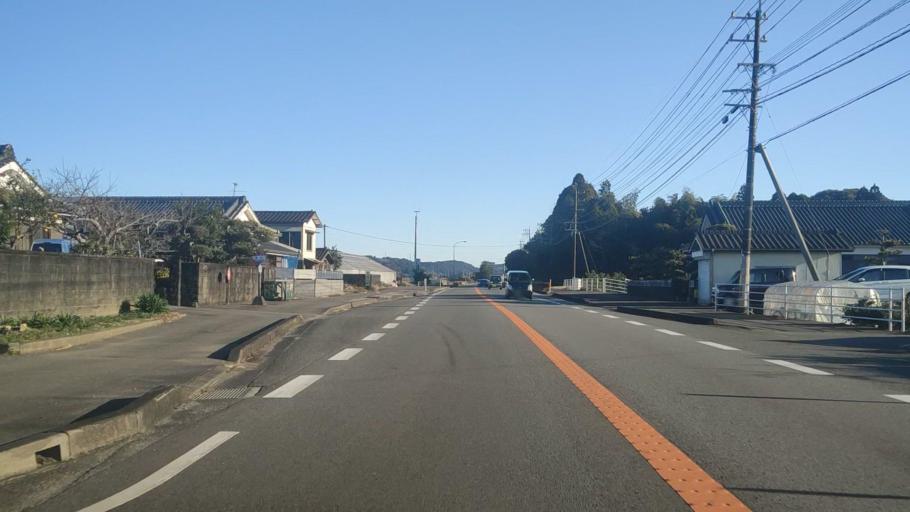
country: JP
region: Miyazaki
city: Takanabe
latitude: 32.3161
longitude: 131.5906
